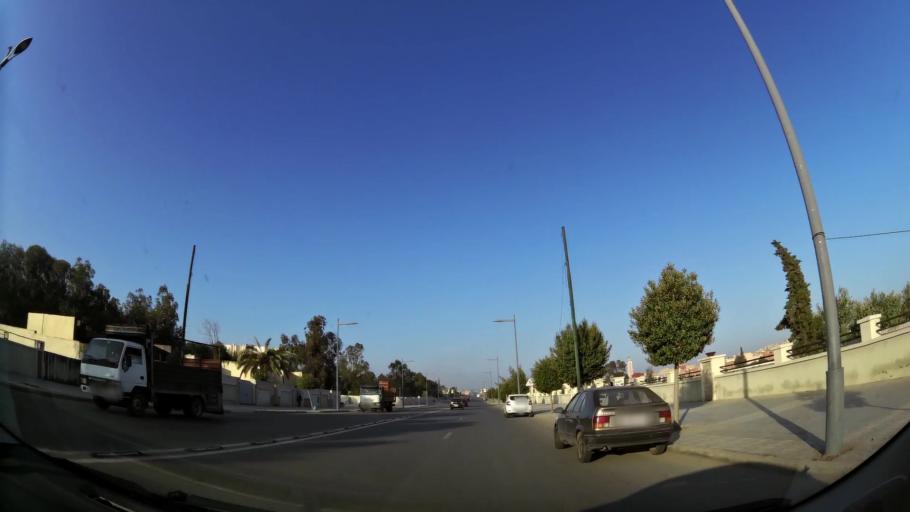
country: MA
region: Oriental
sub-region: Oujda-Angad
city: Oujda
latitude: 34.6727
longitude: -1.9336
